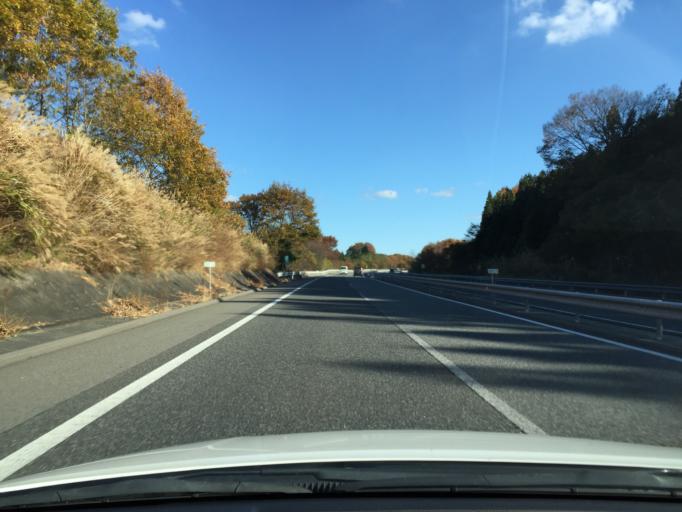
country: JP
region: Fukushima
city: Funehikimachi-funehiki
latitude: 37.2685
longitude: 140.6377
